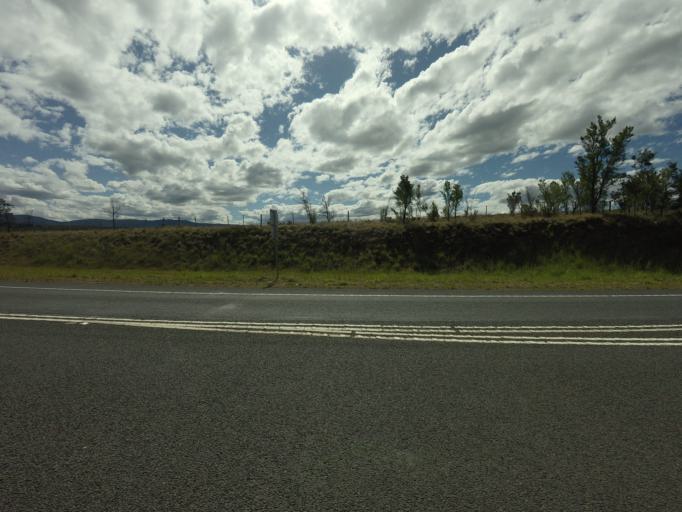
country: AU
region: Tasmania
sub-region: Northern Midlands
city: Evandale
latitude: -42.1306
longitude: 147.4291
